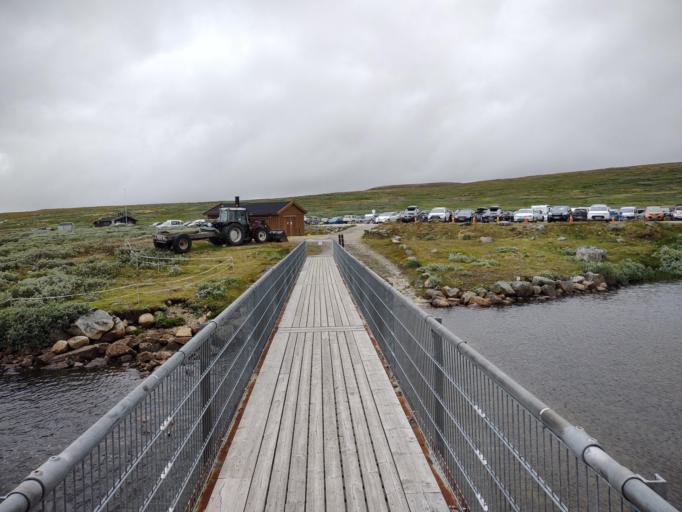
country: NO
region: Hordaland
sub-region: Eidfjord
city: Eidfjord
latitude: 60.2867
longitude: 7.5608
